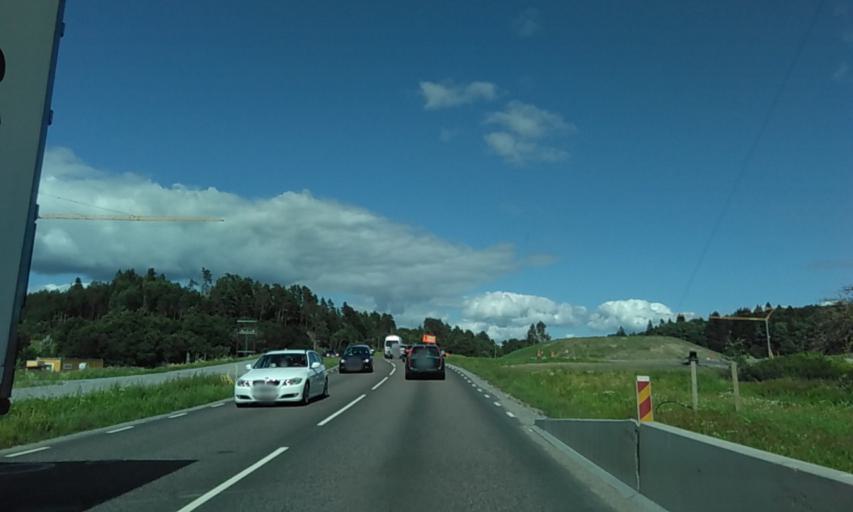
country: SE
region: Vaestra Goetaland
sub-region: Alingsas Kommun
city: Alingsas
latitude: 57.9417
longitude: 12.5868
